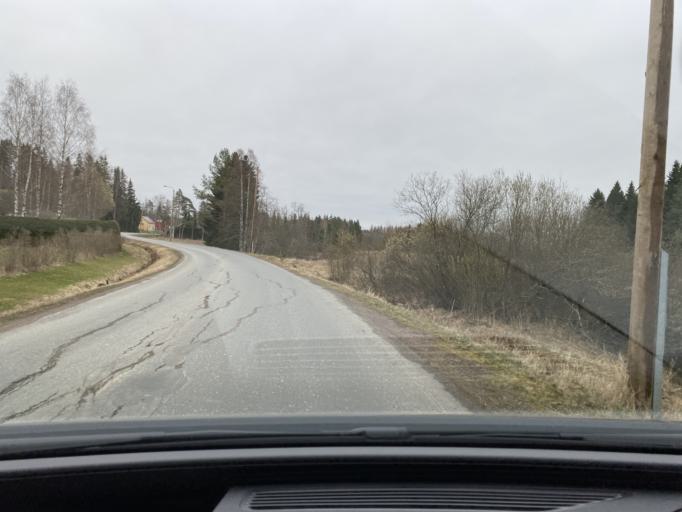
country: FI
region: Satakunta
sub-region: Pori
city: Huittinen
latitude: 61.1641
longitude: 22.7262
